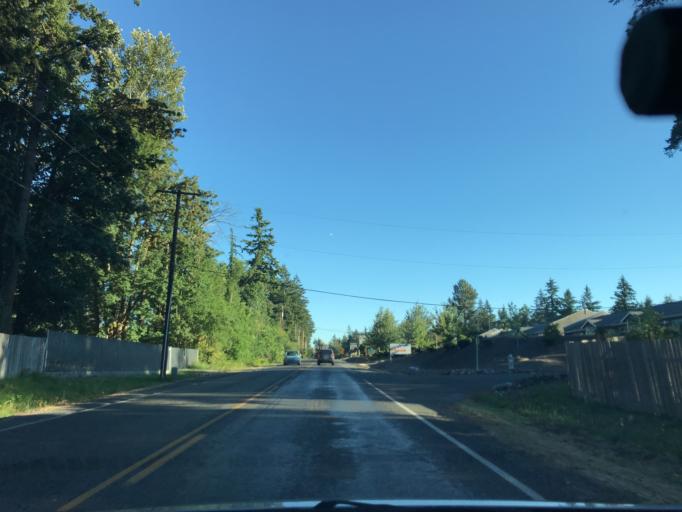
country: US
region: Washington
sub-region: King County
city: Pacific
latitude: 47.2562
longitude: -122.1868
